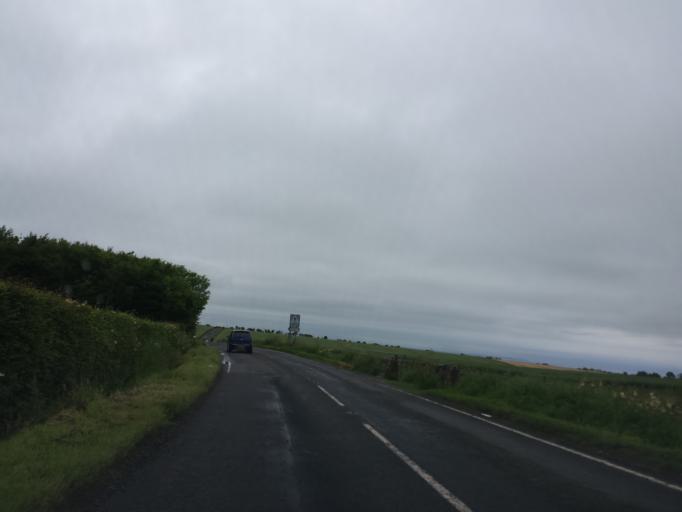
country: GB
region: Scotland
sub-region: Fife
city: Strathkinness
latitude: 56.2945
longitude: -2.8299
